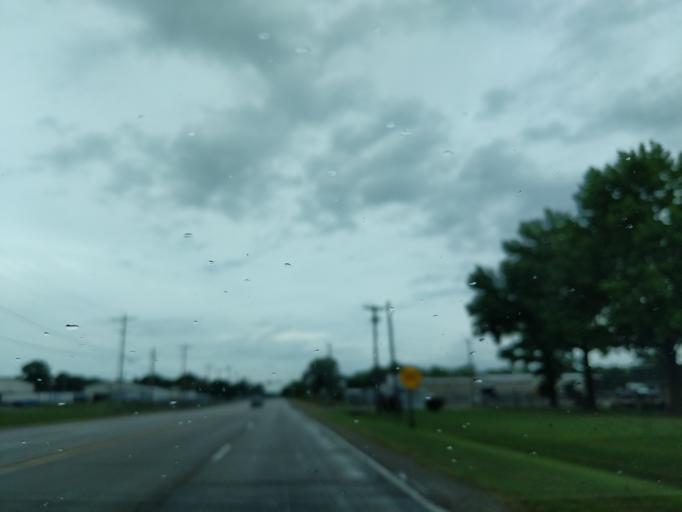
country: US
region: Illinois
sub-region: Saint Clair County
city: Fairmont City
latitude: 38.6592
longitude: -90.0774
